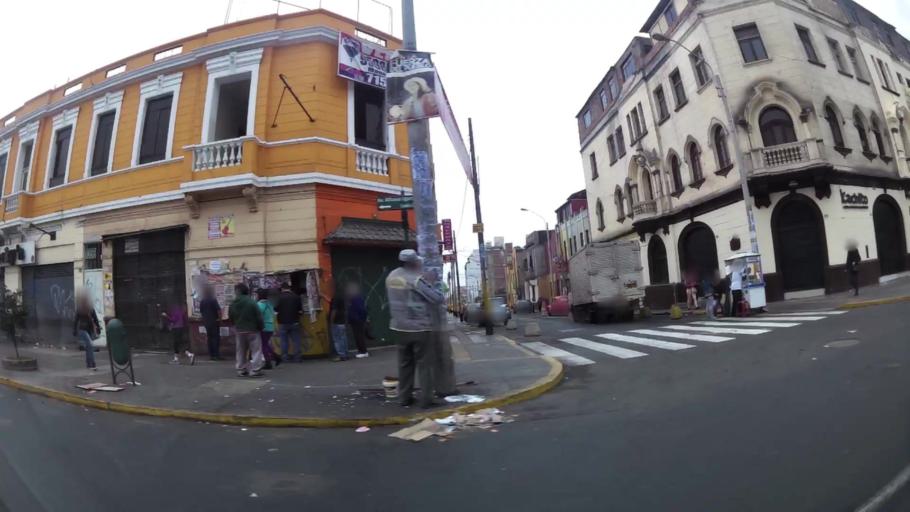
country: PE
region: Lima
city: Lima
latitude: -12.0572
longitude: -77.0420
